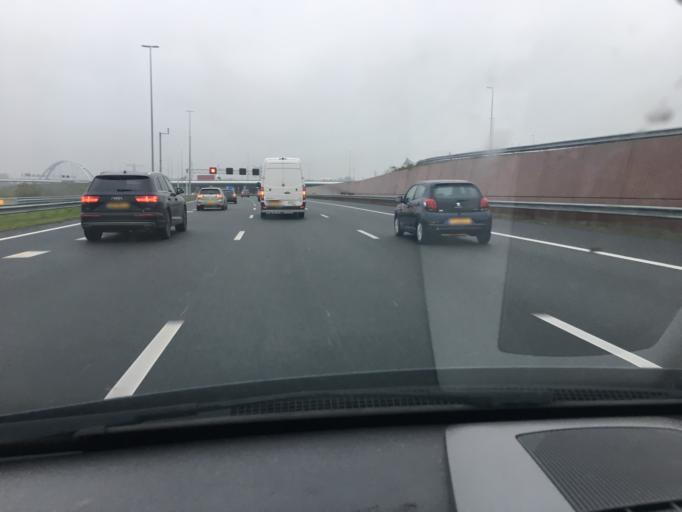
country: NL
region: North Holland
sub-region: Gemeente Naarden
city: Naarden
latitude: 52.3126
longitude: 5.1166
